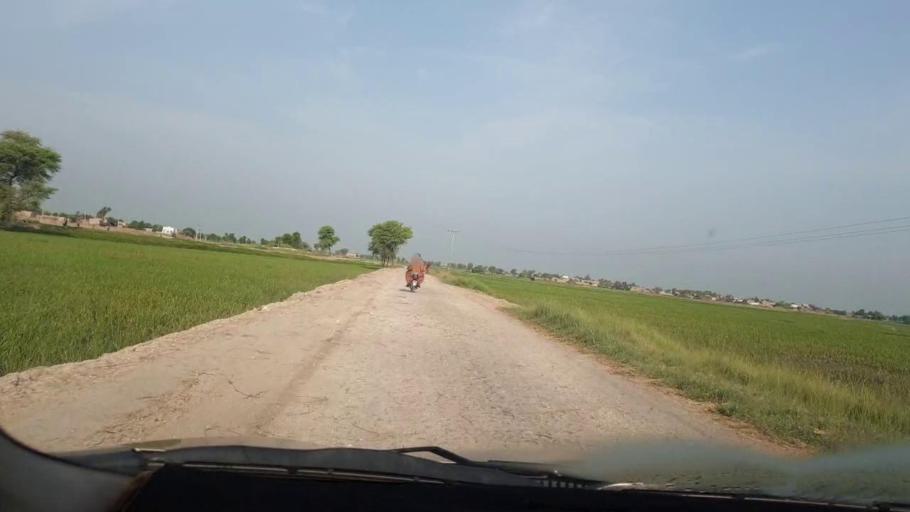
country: PK
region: Sindh
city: Goth Garelo
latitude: 27.4833
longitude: 68.0735
